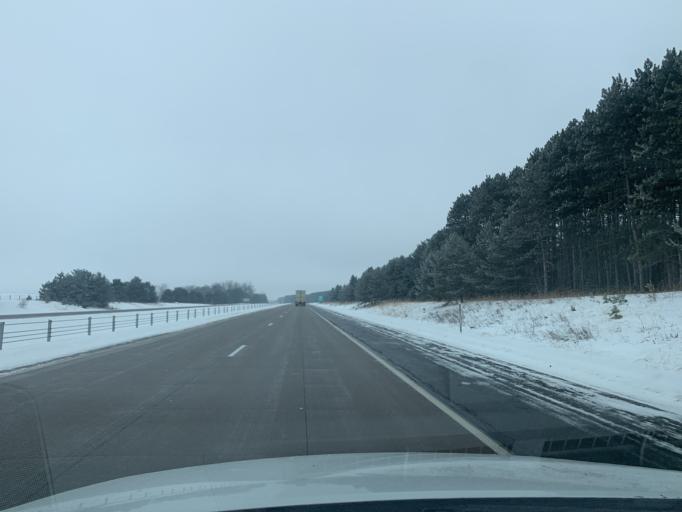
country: US
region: Minnesota
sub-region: Chisago County
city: Harris
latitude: 45.5562
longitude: -92.9905
